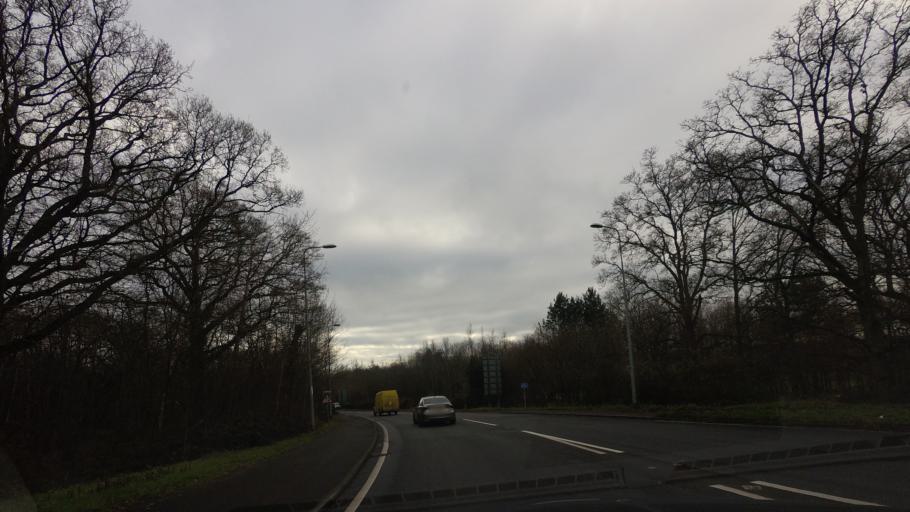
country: GB
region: England
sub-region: East Sussex
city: Wadhurst
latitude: 51.0908
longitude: 0.3961
